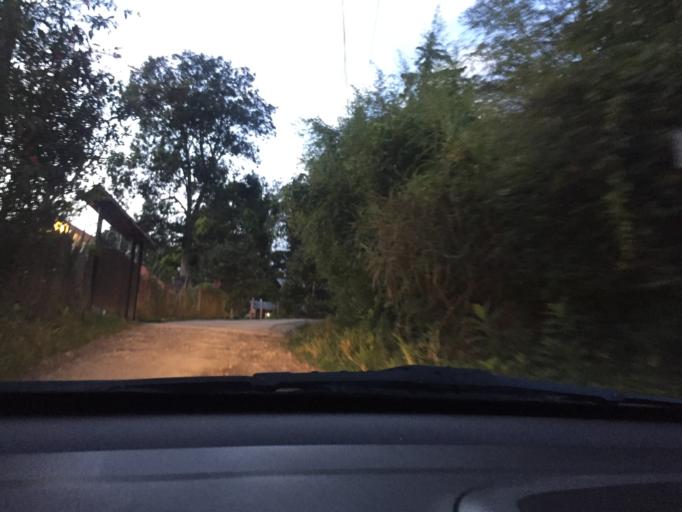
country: CO
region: Cundinamarca
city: Zipacon
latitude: 4.7185
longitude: -74.4145
